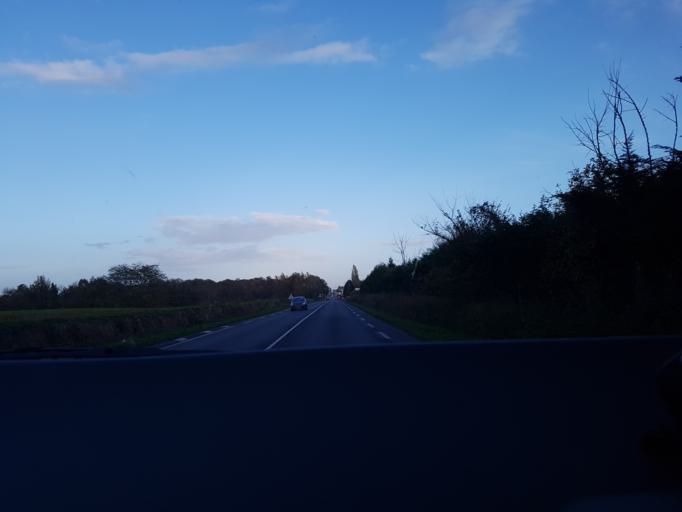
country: FR
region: Lower Normandy
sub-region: Departement du Calvados
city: Giberville
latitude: 49.1720
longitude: -0.2909
